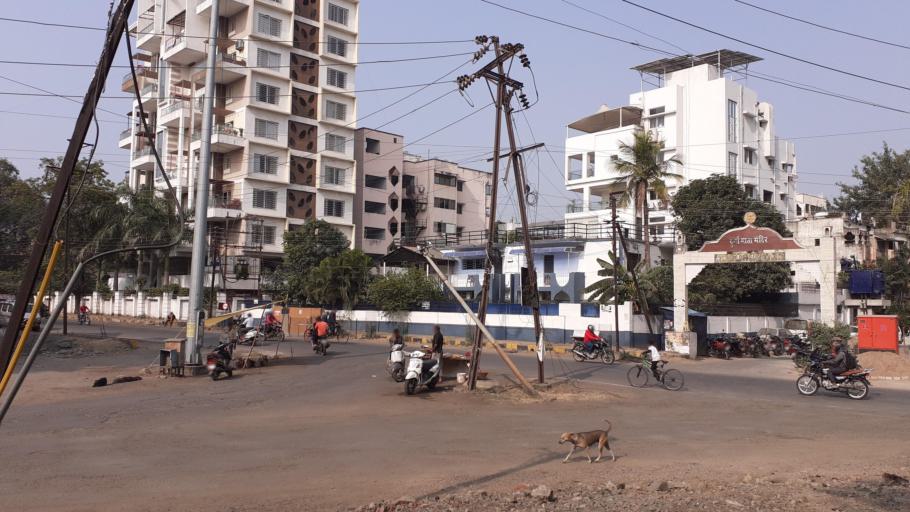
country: IN
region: Maharashtra
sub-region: Nagpur Division
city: Nagpur
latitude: 21.1666
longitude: 79.0830
